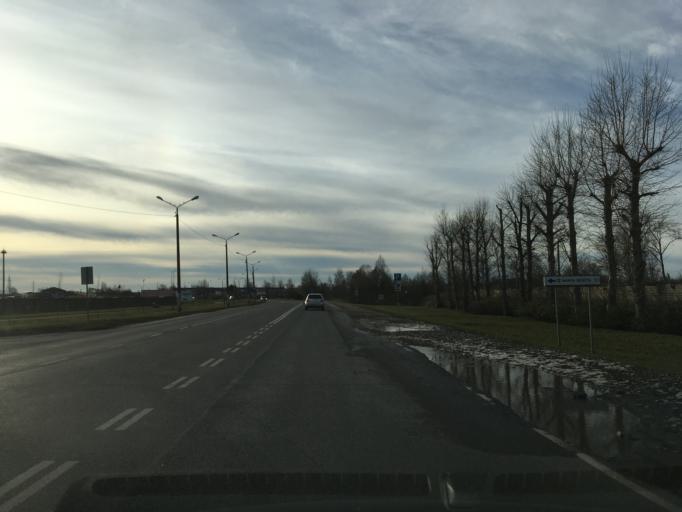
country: EE
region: Ida-Virumaa
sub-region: Narva linn
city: Narva
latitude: 59.3795
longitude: 28.1556
